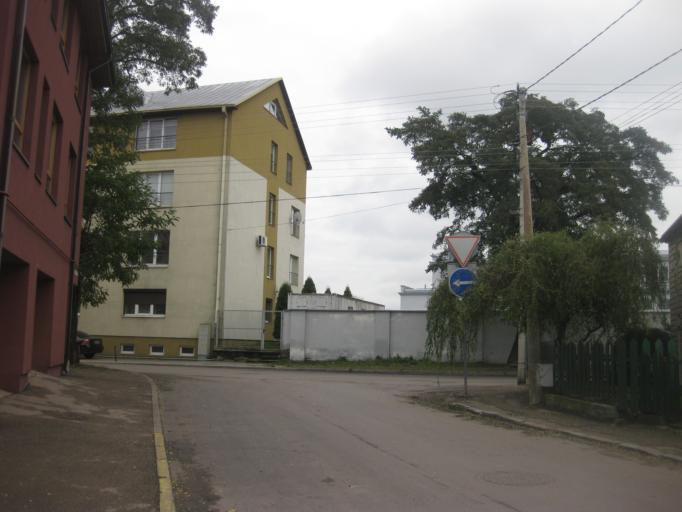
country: LT
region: Kauno apskritis
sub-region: Kaunas
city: Kaunas
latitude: 54.9094
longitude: 23.9143
